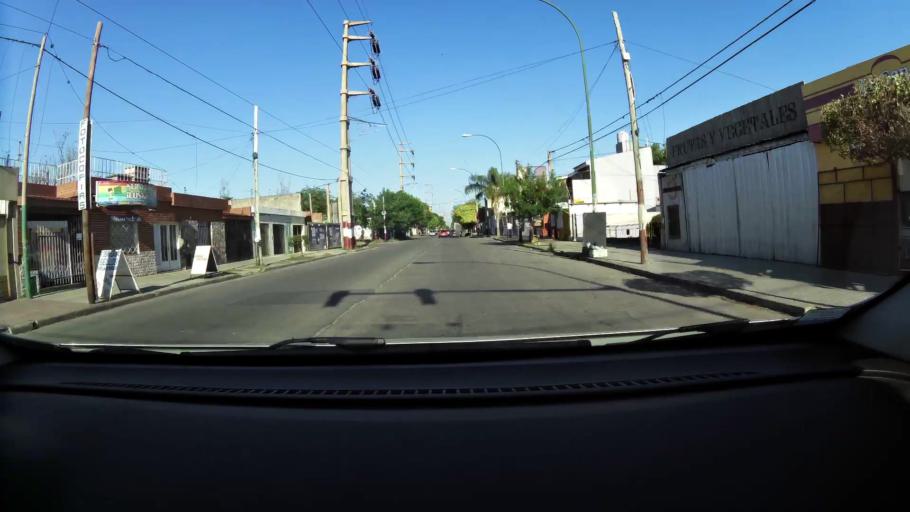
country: AR
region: Cordoba
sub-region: Departamento de Capital
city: Cordoba
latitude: -31.3805
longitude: -64.1877
